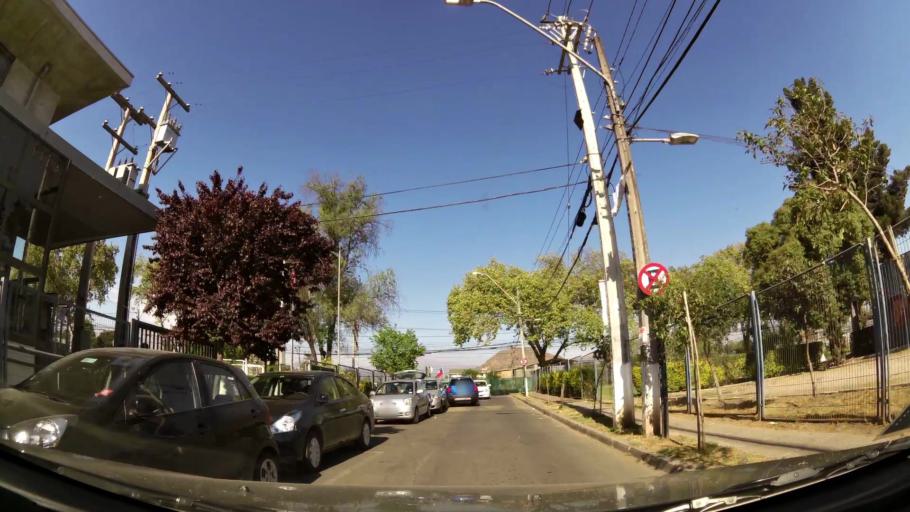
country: CL
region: Santiago Metropolitan
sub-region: Provincia de Maipo
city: San Bernardo
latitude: -33.6143
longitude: -70.6978
